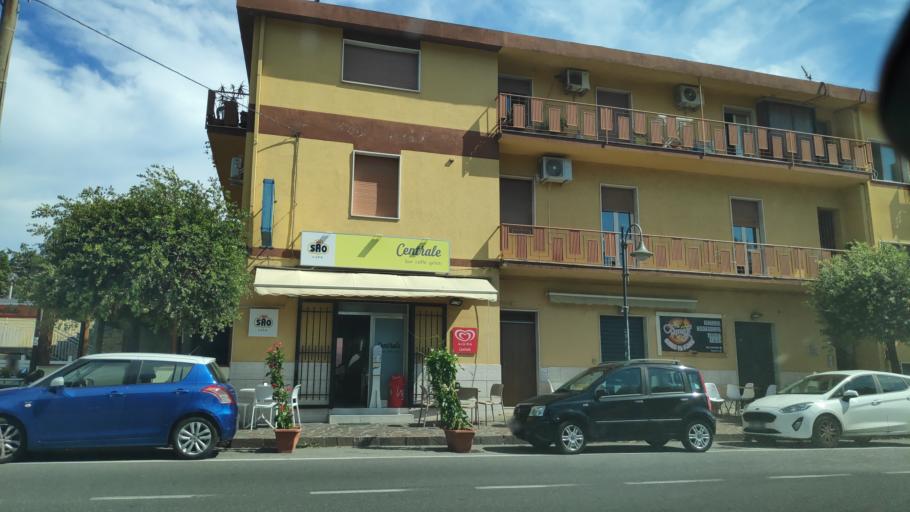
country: IT
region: Calabria
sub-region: Provincia di Catanzaro
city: Montepaone Lido
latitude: 38.7286
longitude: 16.5413
